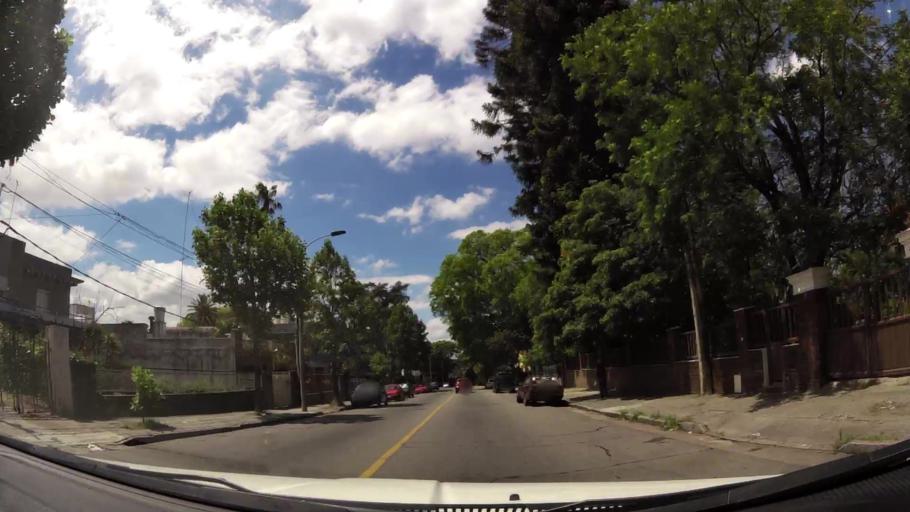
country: UY
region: Montevideo
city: Montevideo
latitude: -34.8528
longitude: -56.2079
